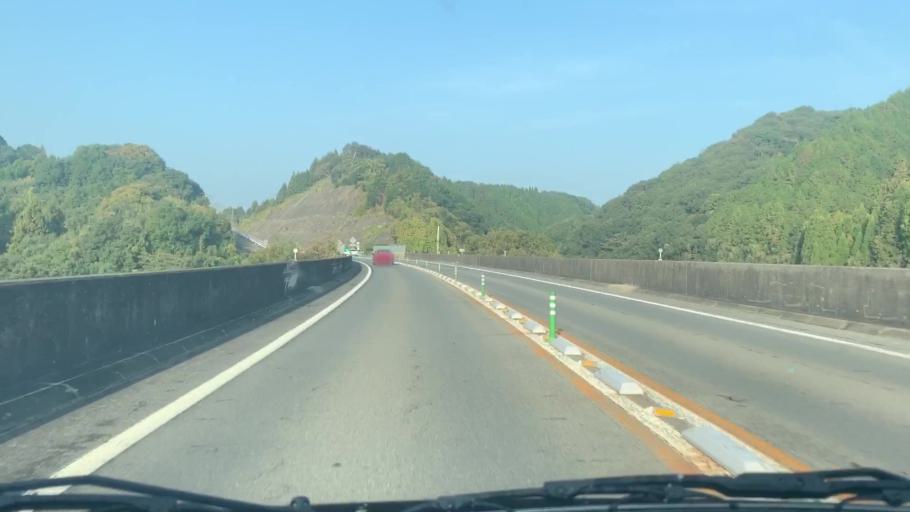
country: JP
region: Saga Prefecture
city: Ureshinomachi-shimojuku
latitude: 33.1469
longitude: 129.9491
